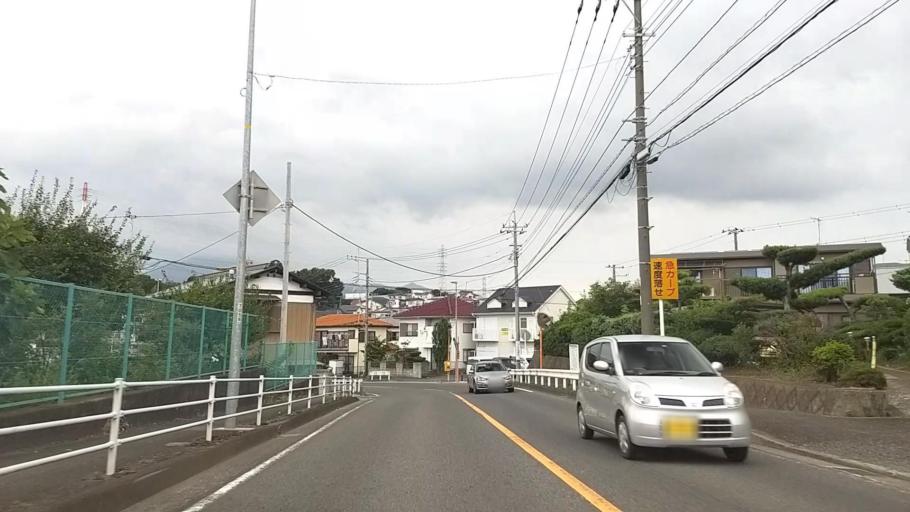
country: JP
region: Kanagawa
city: Isehara
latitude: 35.3893
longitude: 139.3265
